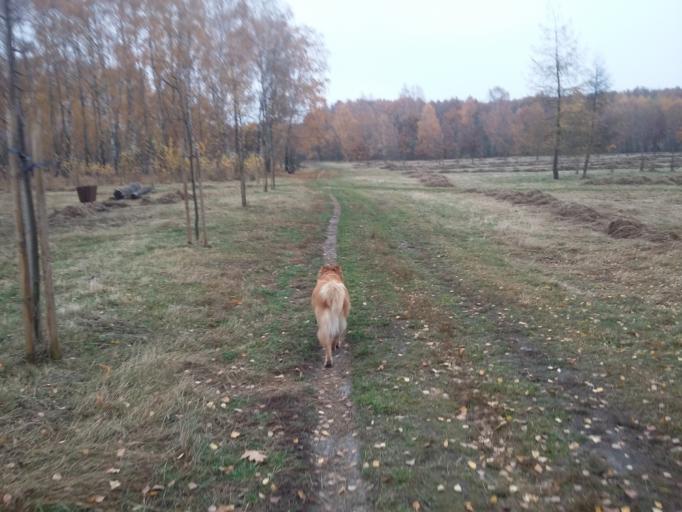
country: PL
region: Lodz Voivodeship
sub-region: Powiat pabianicki
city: Ksawerow
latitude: 51.7302
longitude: 19.3858
